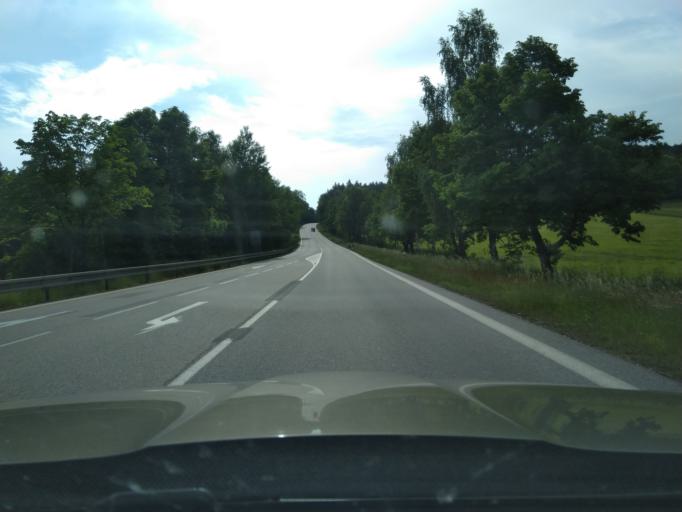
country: CZ
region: Jihocesky
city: Vlachovo Brezi
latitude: 49.0575
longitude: 13.9467
